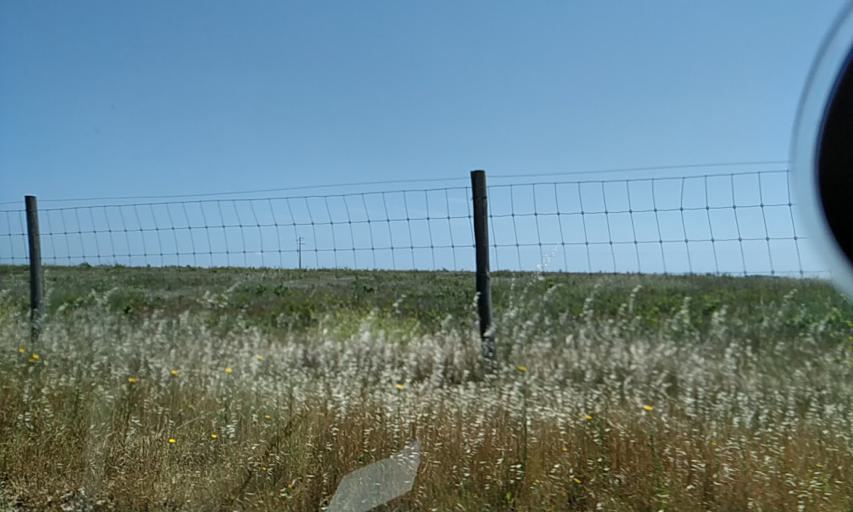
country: PT
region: Setubal
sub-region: Palmela
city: Palmela
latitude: 38.6007
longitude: -8.8277
